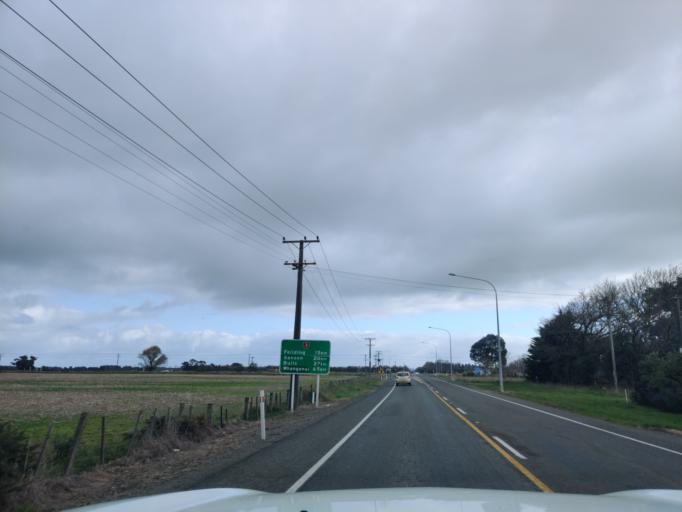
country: NZ
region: Manawatu-Wanganui
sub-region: Palmerston North City
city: Palmerston North
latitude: -40.3345
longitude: 175.5924
